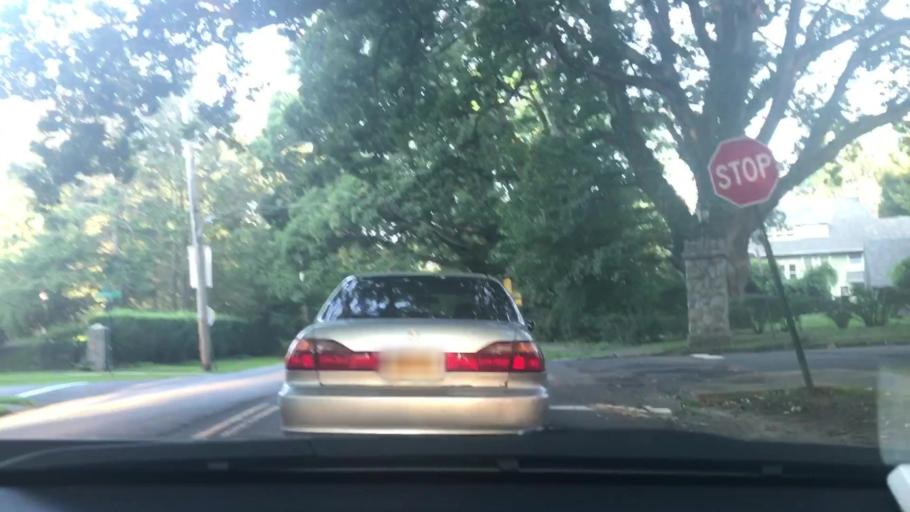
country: US
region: New York
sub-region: Westchester County
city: Pelham Manor
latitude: 40.9025
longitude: -73.8029
